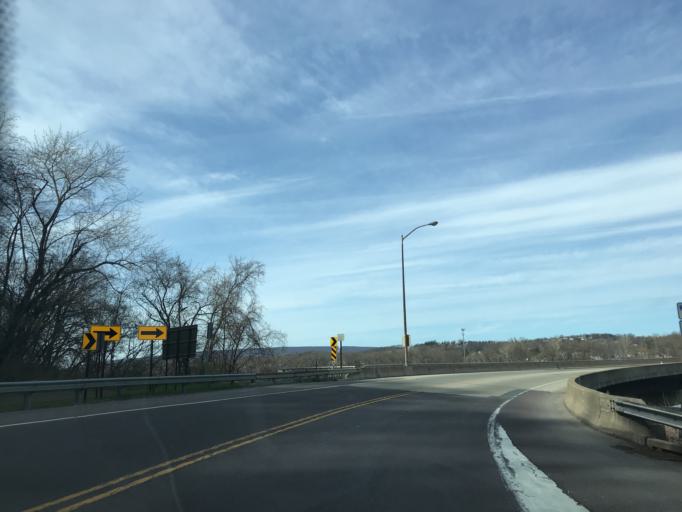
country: US
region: Pennsylvania
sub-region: Northumberland County
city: Northumberland
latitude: 40.8815
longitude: -76.8003
